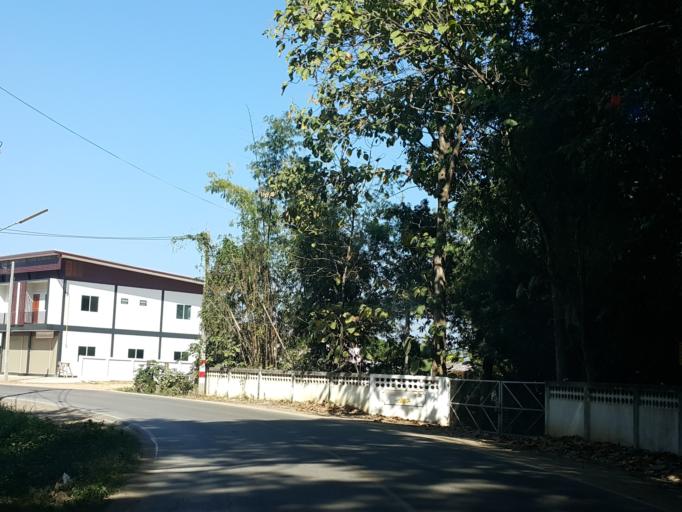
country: TH
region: Chiang Mai
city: San Sai
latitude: 18.8674
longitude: 98.9831
